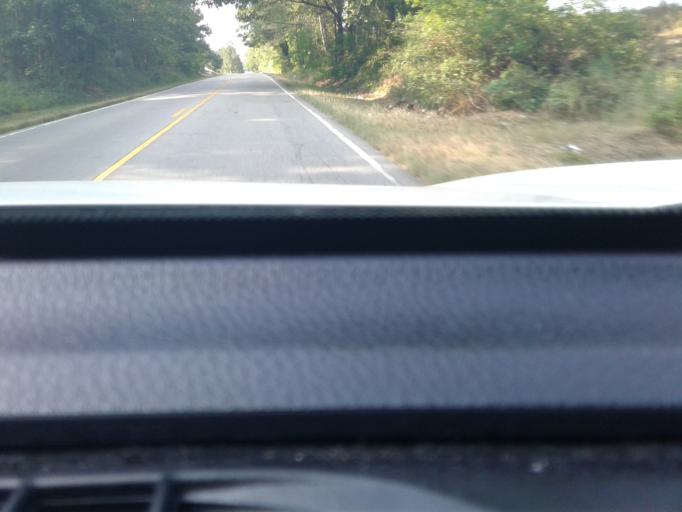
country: US
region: North Carolina
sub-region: Johnston County
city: Benson
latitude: 35.4131
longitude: -78.5402
